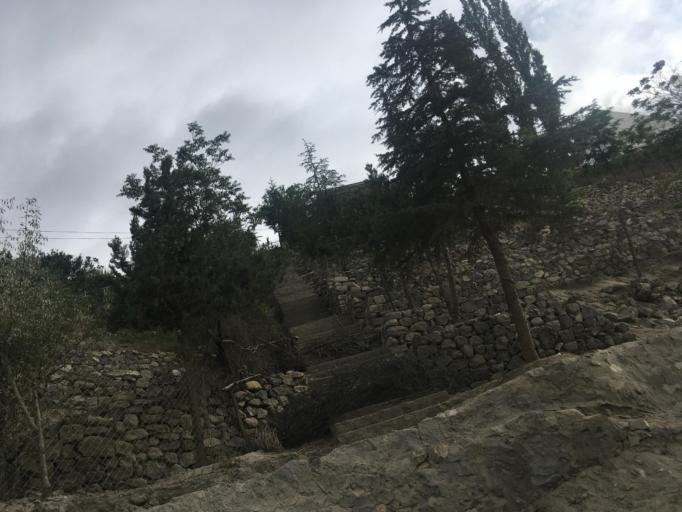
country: PK
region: Gilgit-Baltistan
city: Skardu
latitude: 35.2961
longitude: 75.6492
